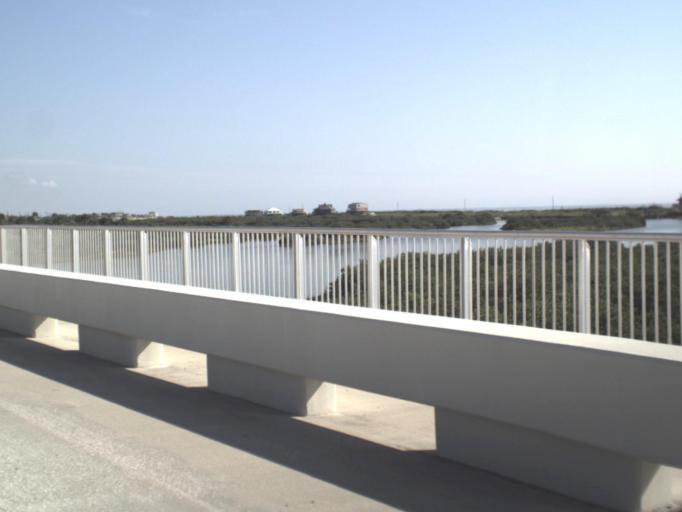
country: US
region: Florida
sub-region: Flagler County
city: Palm Coast
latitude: 29.6792
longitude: -81.2205
